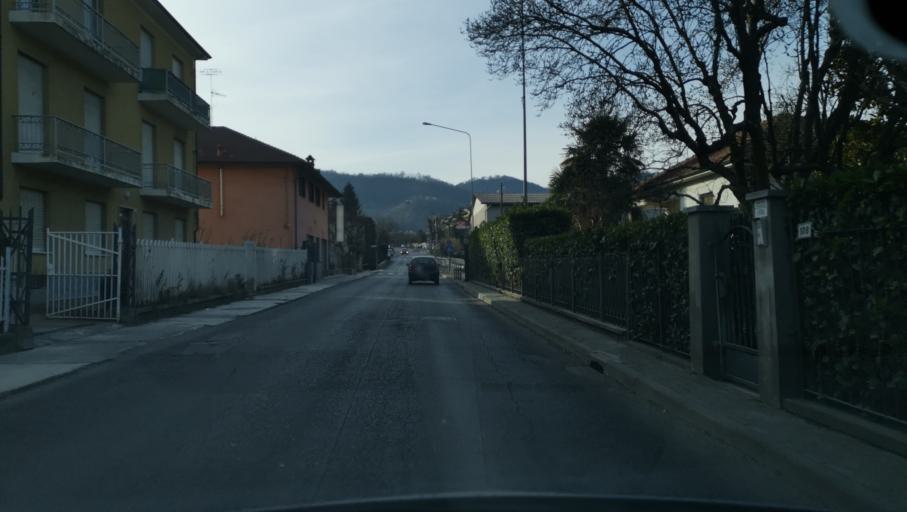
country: IT
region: Piedmont
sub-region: Provincia di Torino
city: Castiglione Torinese
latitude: 45.1135
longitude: 7.8163
